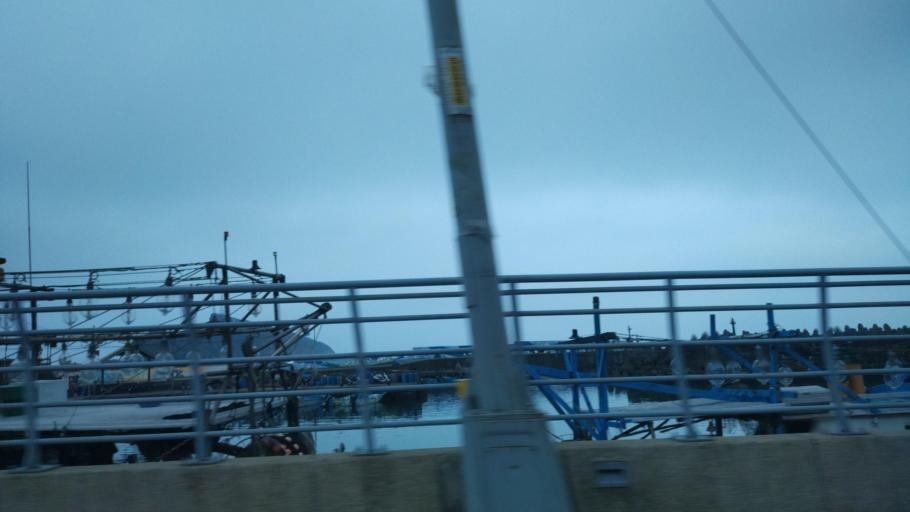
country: TW
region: Taiwan
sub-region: Keelung
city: Keelung
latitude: 25.2035
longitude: 121.6916
